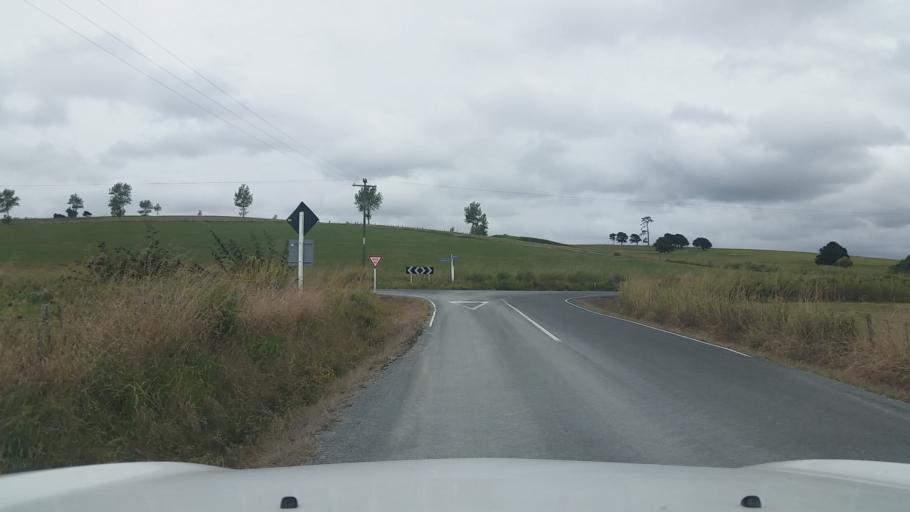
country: NZ
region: Northland
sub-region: Whangarei
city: Maungatapere
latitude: -35.7060
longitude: 174.1452
